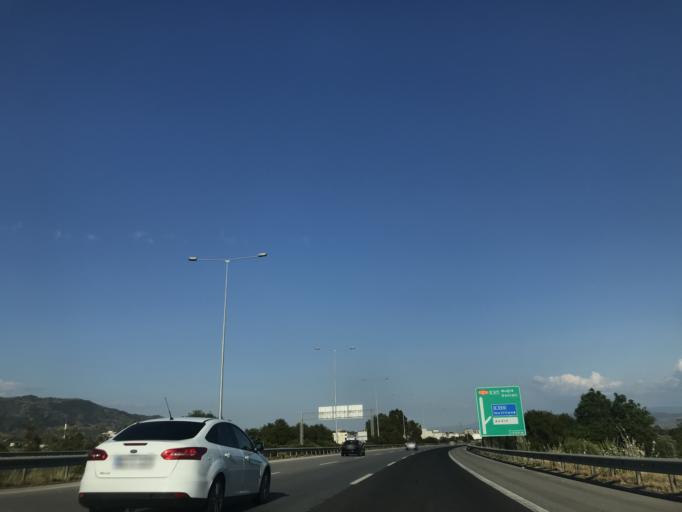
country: TR
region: Aydin
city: Aydin
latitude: 37.8591
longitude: 27.7948
